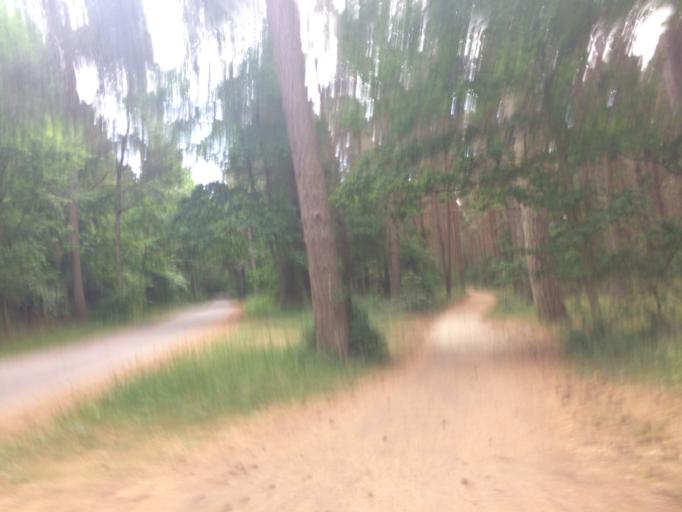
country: DK
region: Capital Region
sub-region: Bornholm Kommune
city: Ronne
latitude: 55.1409
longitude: 14.7158
